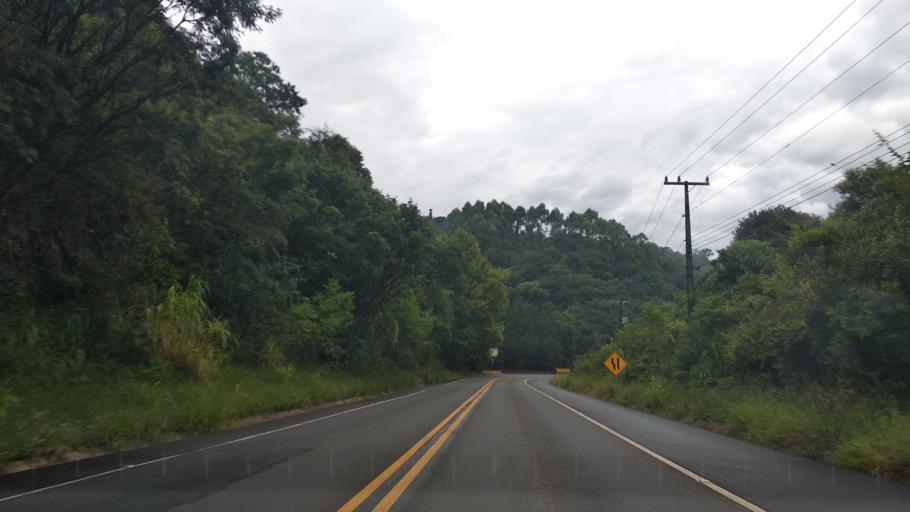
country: BR
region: Santa Catarina
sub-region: Videira
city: Videira
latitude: -27.0612
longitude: -51.2253
